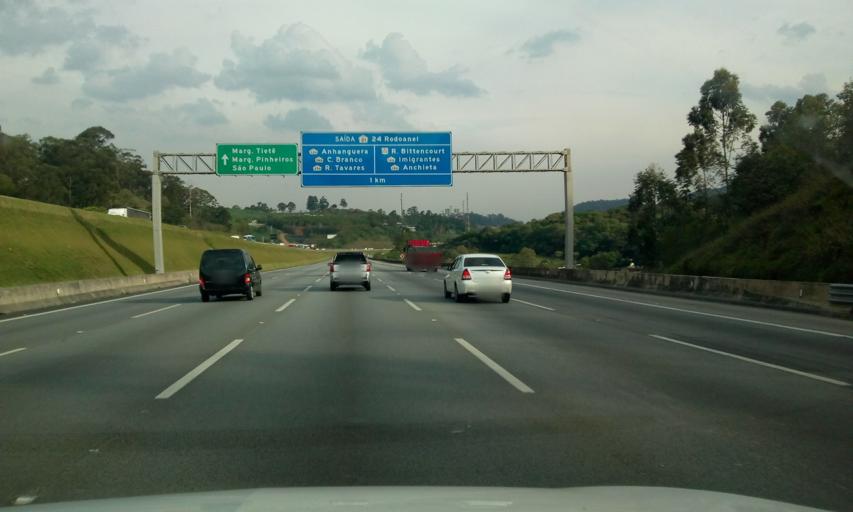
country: BR
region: Sao Paulo
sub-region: Caieiras
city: Caieiras
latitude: -23.4179
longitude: -46.7641
